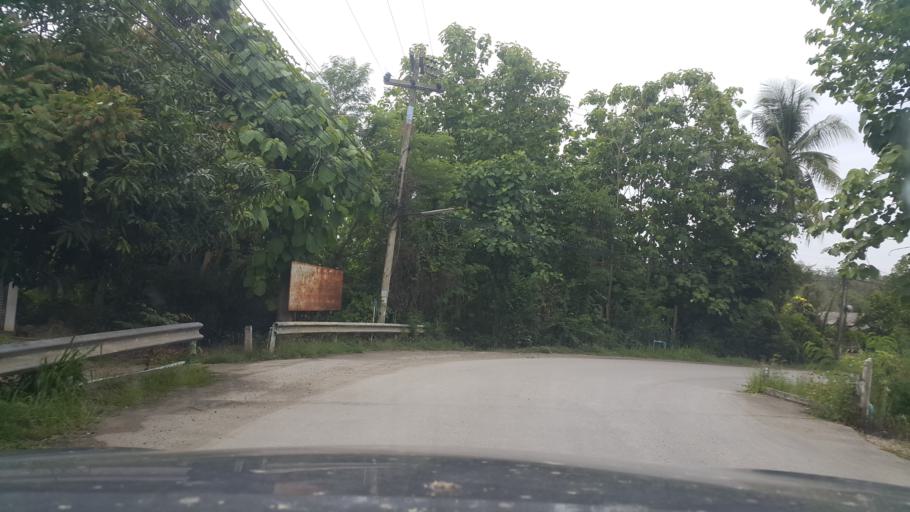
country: TH
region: Chiang Mai
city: San Pa Tong
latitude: 18.6659
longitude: 98.8356
